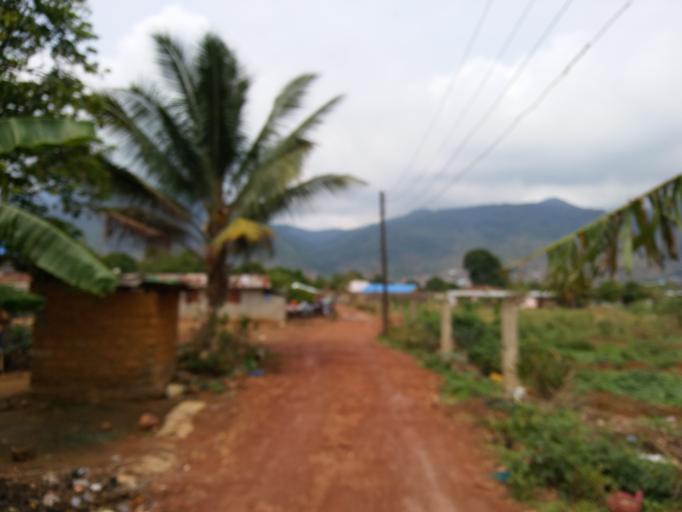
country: SL
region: Western Area
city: Hastings
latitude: 8.3866
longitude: -13.1478
